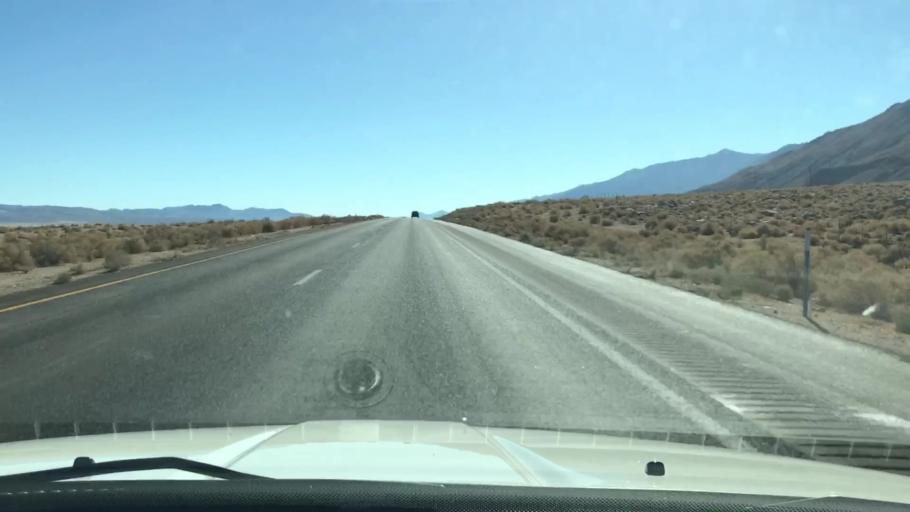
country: US
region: California
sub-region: Inyo County
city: Lone Pine
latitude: 36.3933
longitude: -118.0247
